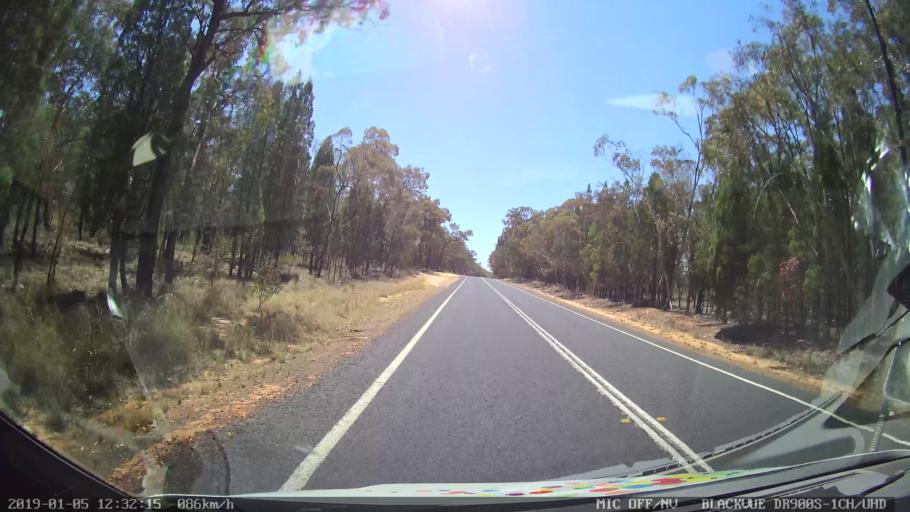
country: AU
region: New South Wales
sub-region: Warrumbungle Shire
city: Coonabarabran
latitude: -31.2178
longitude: 149.3769
